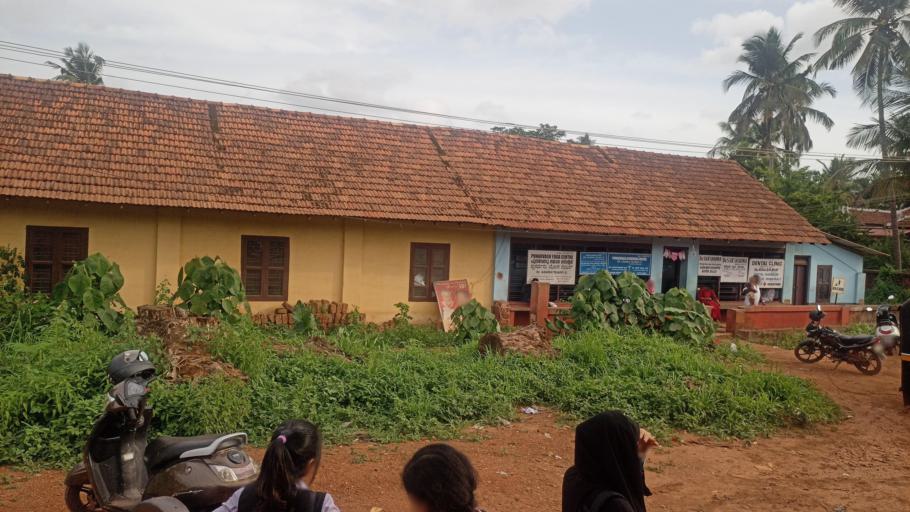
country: IN
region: Kerala
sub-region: Kasaragod District
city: Kasaragod
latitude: 12.5176
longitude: 75.0151
